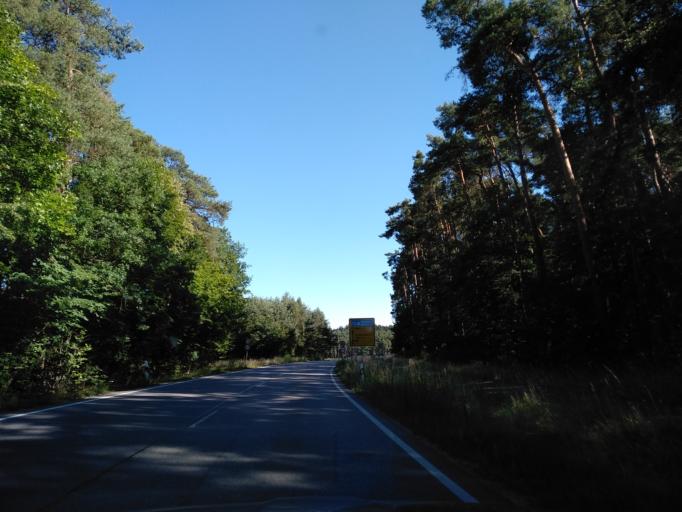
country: DE
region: Bavaria
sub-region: Regierungsbezirk Mittelfranken
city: Rottenbach
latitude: 49.6493
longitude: 10.9194
